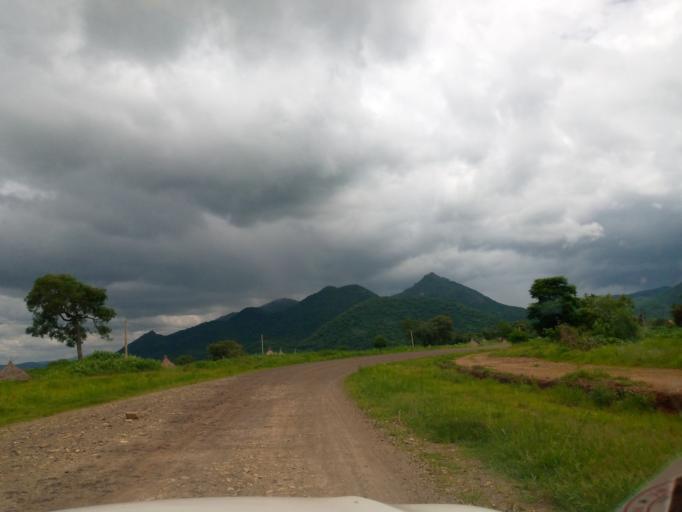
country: ET
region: Oromiya
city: Mendi
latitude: 10.1806
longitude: 35.0924
